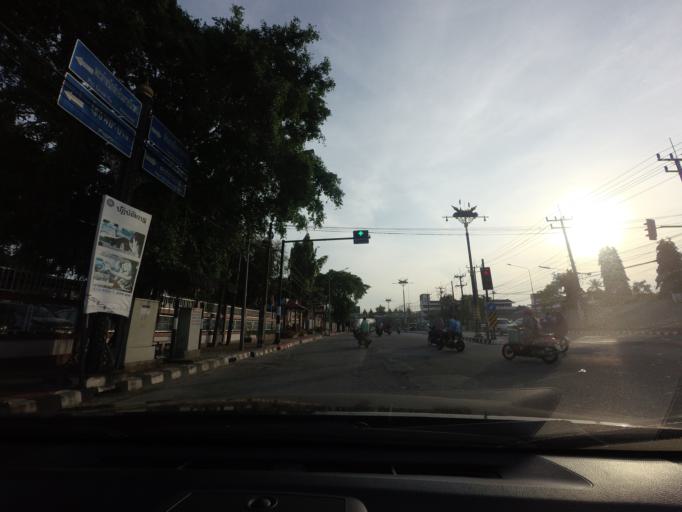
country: TH
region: Narathiwat
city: Narathiwat
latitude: 6.4250
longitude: 101.8240
